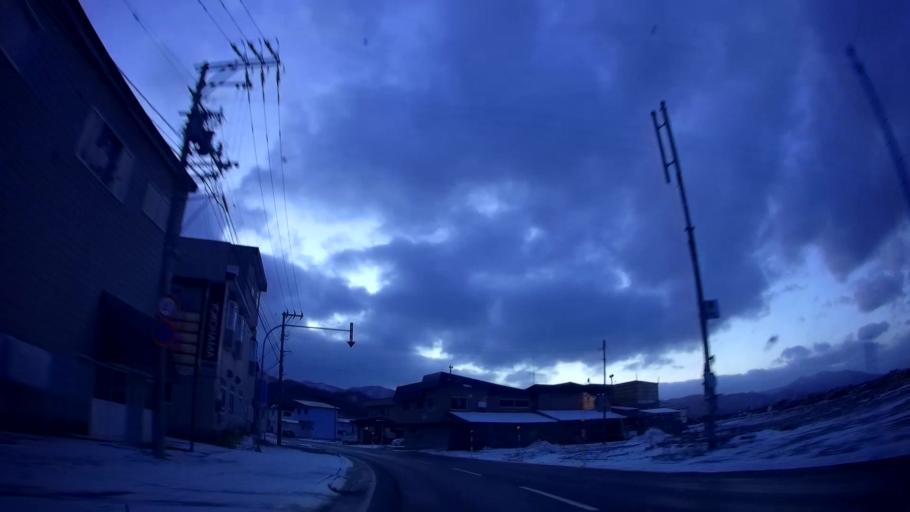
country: JP
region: Hokkaido
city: Hakodate
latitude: 41.8949
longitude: 141.0322
